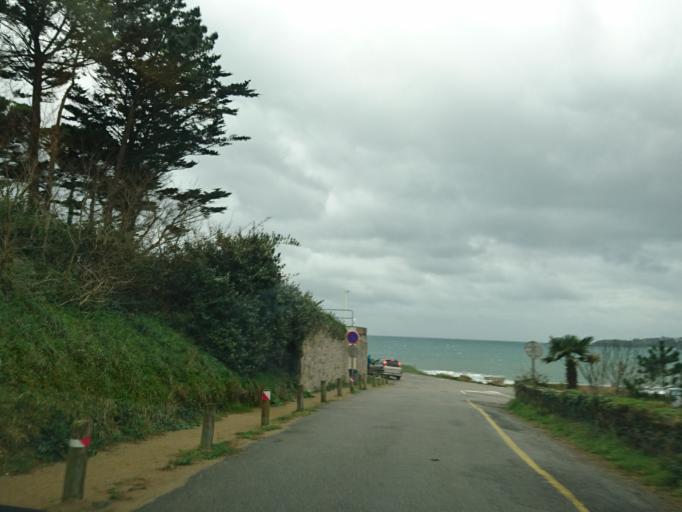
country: FR
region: Brittany
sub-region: Departement du Finistere
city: Plougonvelin
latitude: 48.3563
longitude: -4.6783
